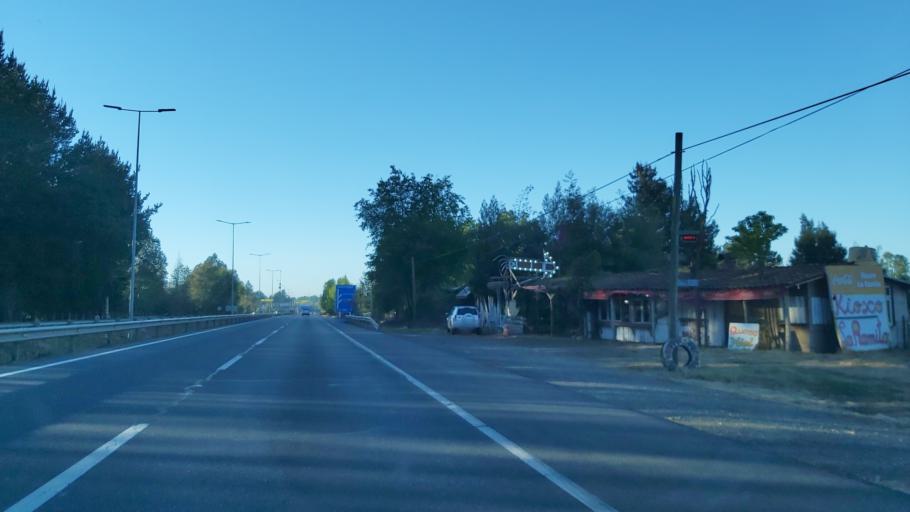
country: CL
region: Araucania
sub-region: Provincia de Malleco
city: Collipulli
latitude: -38.0720
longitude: -72.3754
